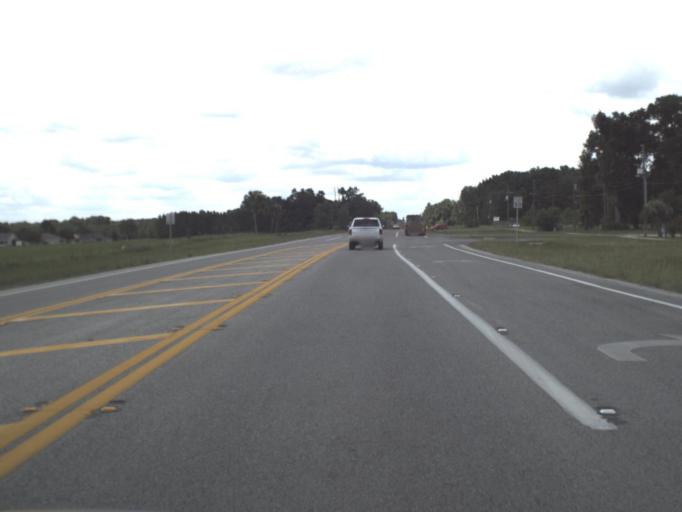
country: US
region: Florida
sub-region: Alachua County
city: Newberry
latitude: 29.6563
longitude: -82.6068
